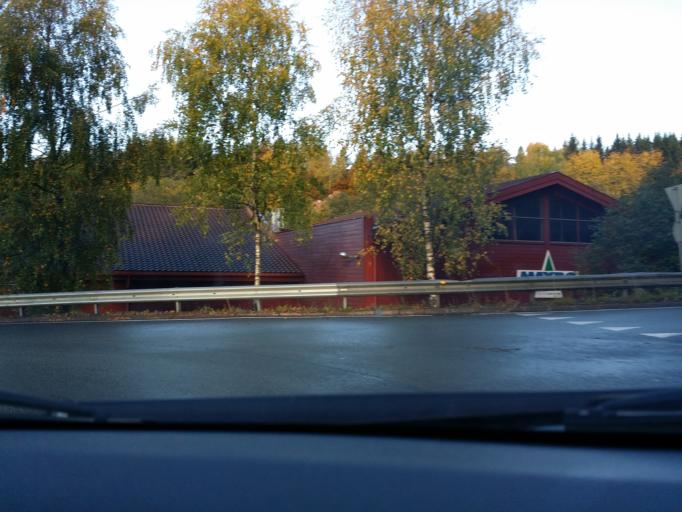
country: NO
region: Akershus
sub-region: Baerum
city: Sandvika
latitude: 59.9441
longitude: 10.5078
